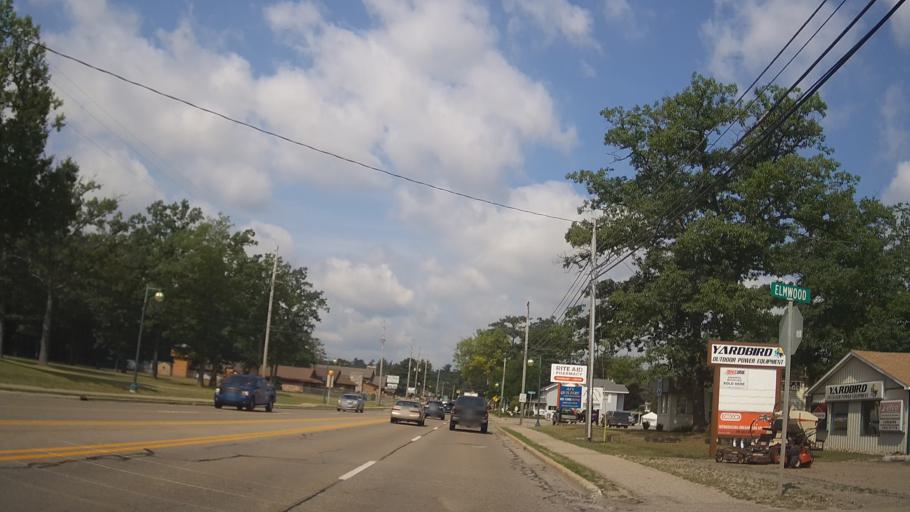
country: US
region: Michigan
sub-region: Roscommon County
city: Houghton Lake
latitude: 44.2983
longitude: -84.7290
